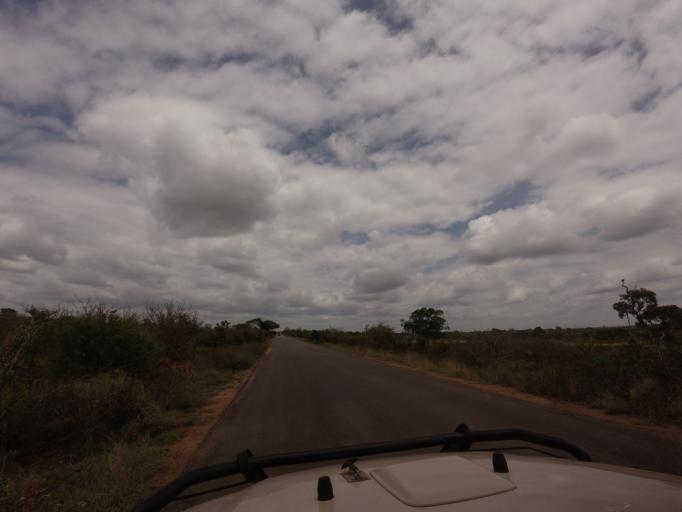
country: ZA
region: Mpumalanga
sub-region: Ehlanzeni District
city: Komatipoort
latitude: -25.1016
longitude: 31.8902
